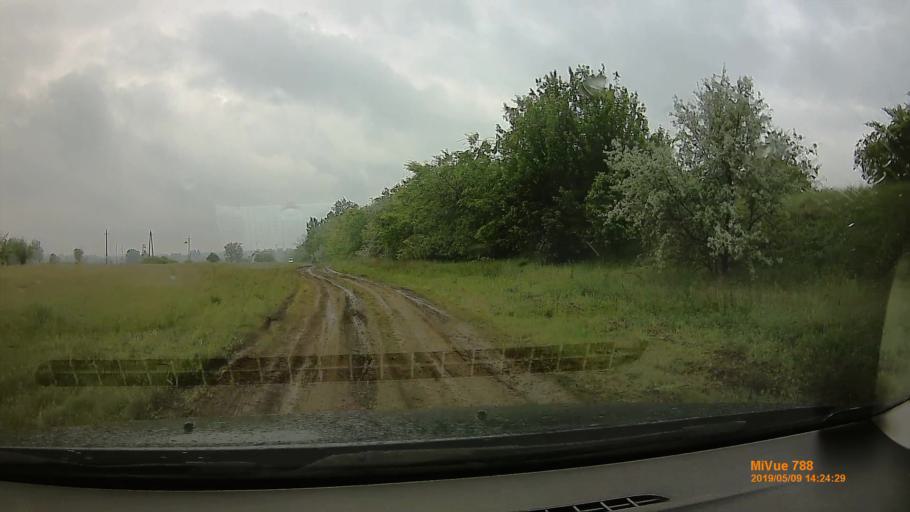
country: HU
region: Budapest
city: Budapest XVI. keruelet
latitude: 47.4997
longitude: 19.2125
